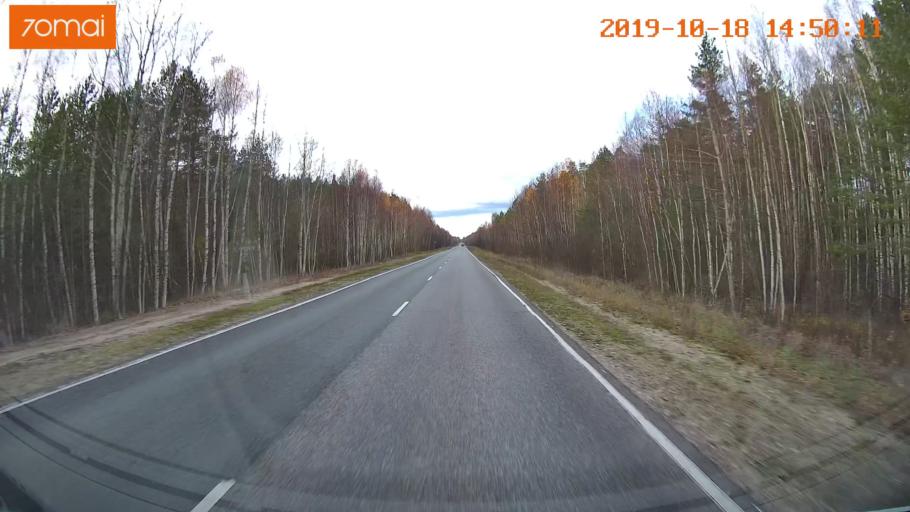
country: RU
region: Vladimir
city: Kurlovo
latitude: 55.4237
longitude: 40.6448
